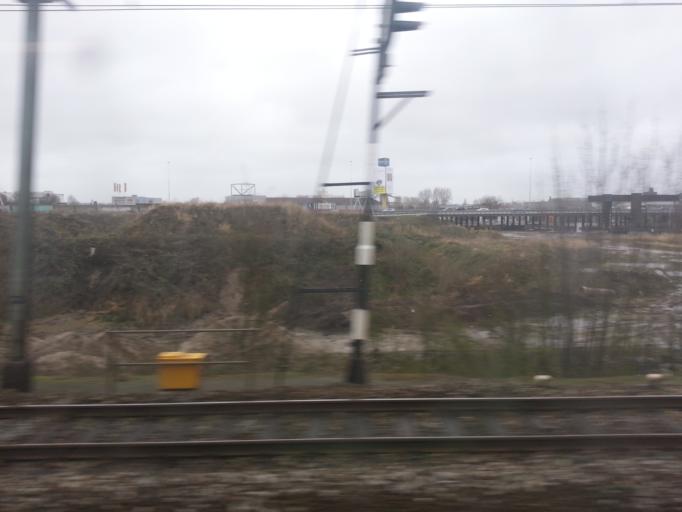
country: NL
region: South Holland
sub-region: Gemeente Schiedam
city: Schiedam
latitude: 51.9233
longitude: 4.4056
